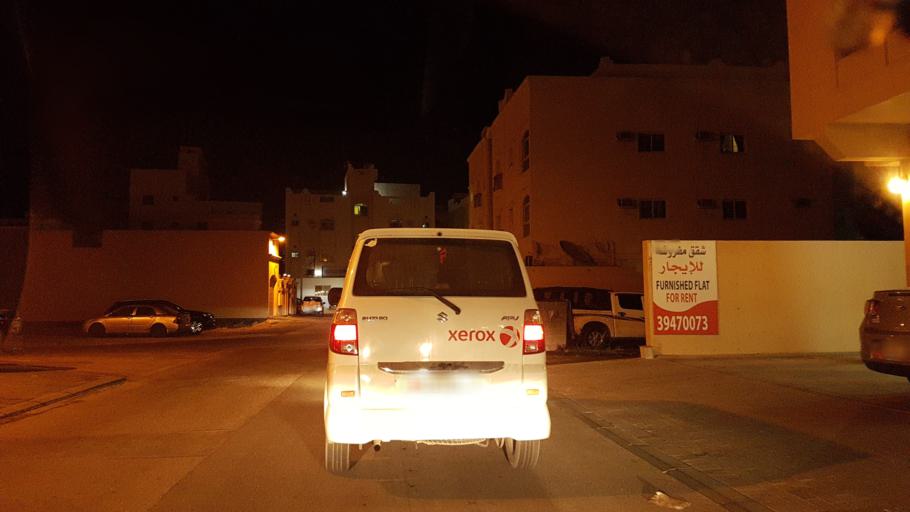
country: BH
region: Manama
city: Jidd Hafs
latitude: 26.2206
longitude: 50.5115
